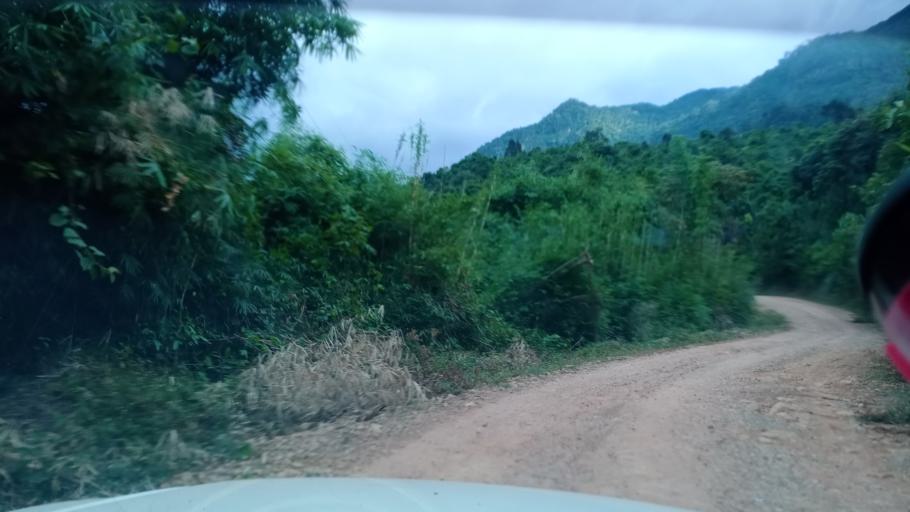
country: TH
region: Changwat Bueng Kan
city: Pak Khat
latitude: 18.7217
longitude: 103.2498
